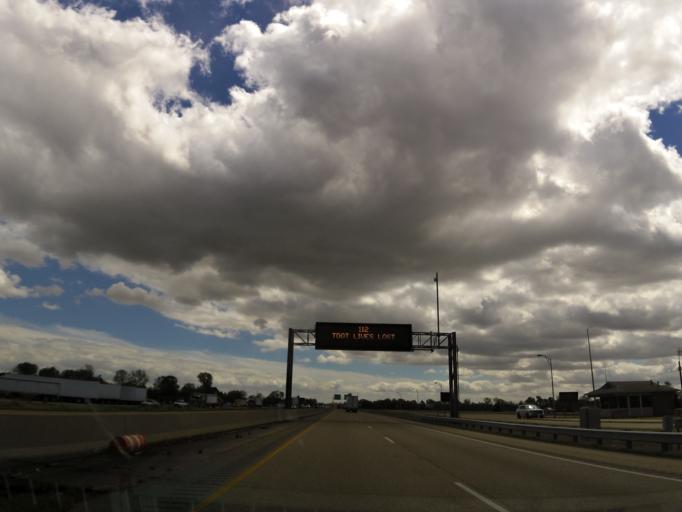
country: US
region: Arkansas
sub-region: Crittenden County
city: Marion
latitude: 35.1928
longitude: -90.2001
